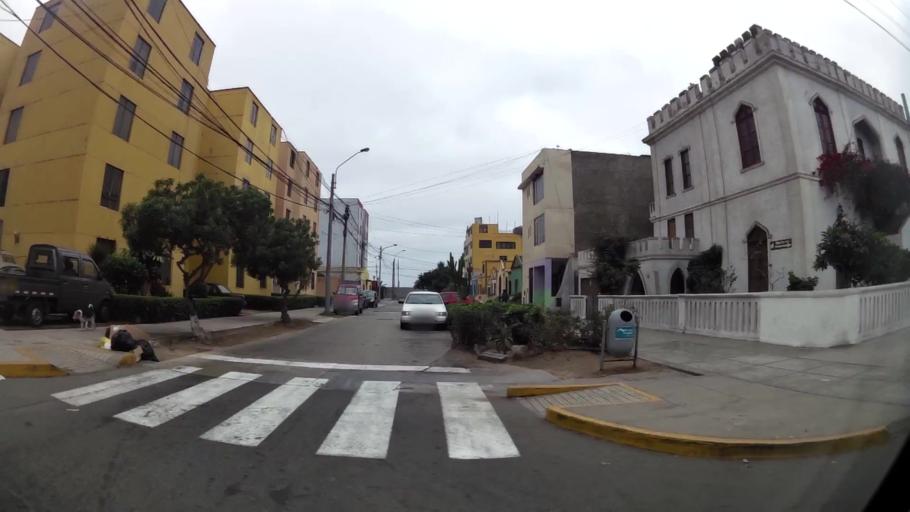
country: PE
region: Lima
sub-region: Lima
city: San Isidro
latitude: -12.0909
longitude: -77.0821
